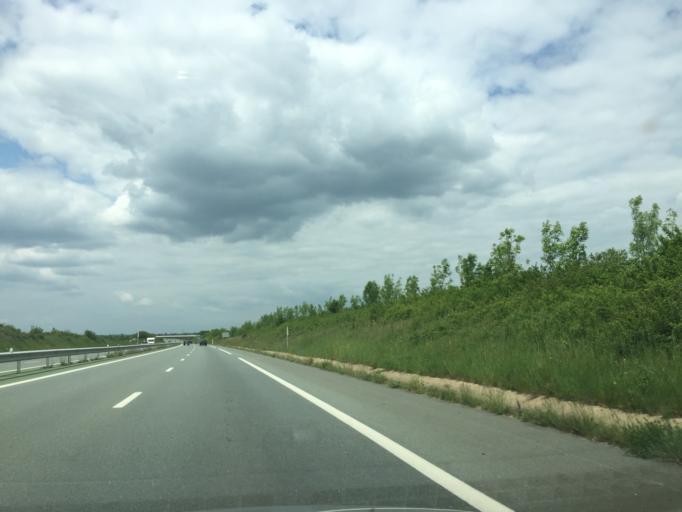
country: FR
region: Poitou-Charentes
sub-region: Departement des Deux-Sevres
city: Saint-Gelais
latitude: 46.4004
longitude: -0.3811
